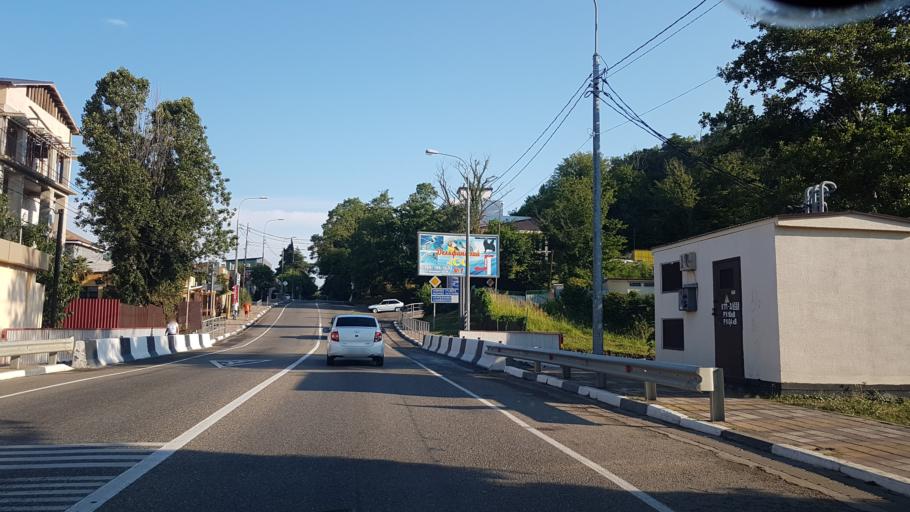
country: RU
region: Krasnodarskiy
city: Gornoye Loo
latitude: 43.6817
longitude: 39.6006
